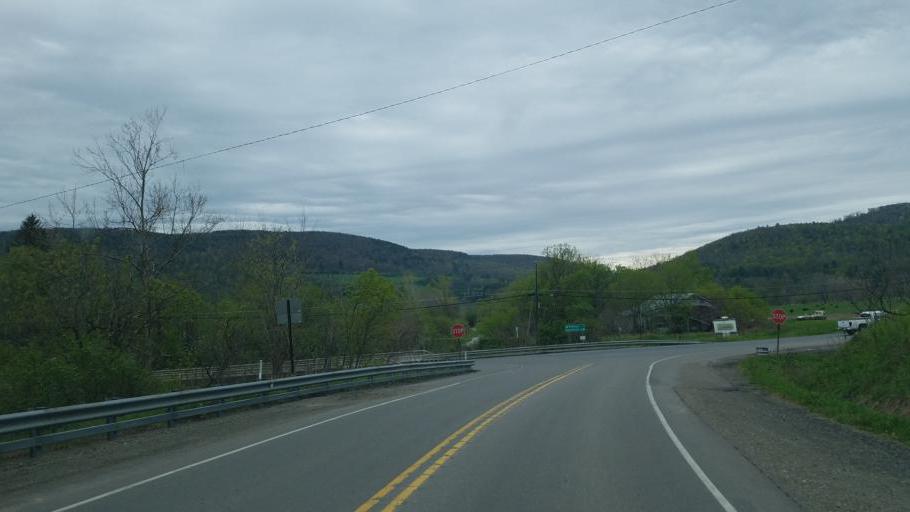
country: US
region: Pennsylvania
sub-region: Tioga County
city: Westfield
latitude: 41.9583
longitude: -77.4446
